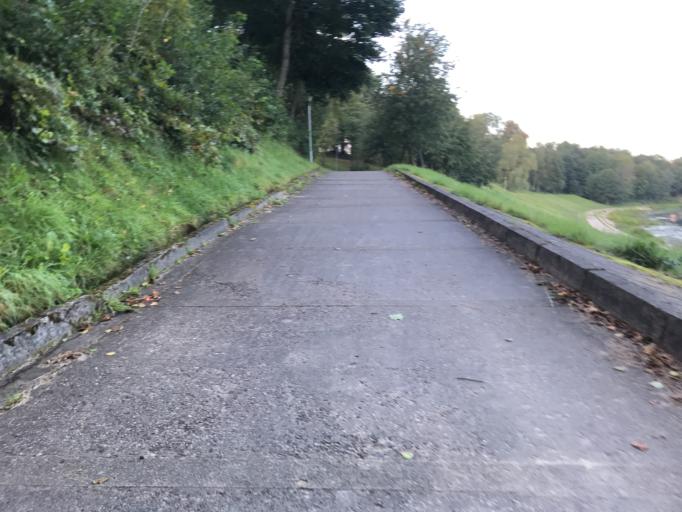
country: LT
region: Alytaus apskritis
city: Druskininkai
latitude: 54.0191
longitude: 23.9873
